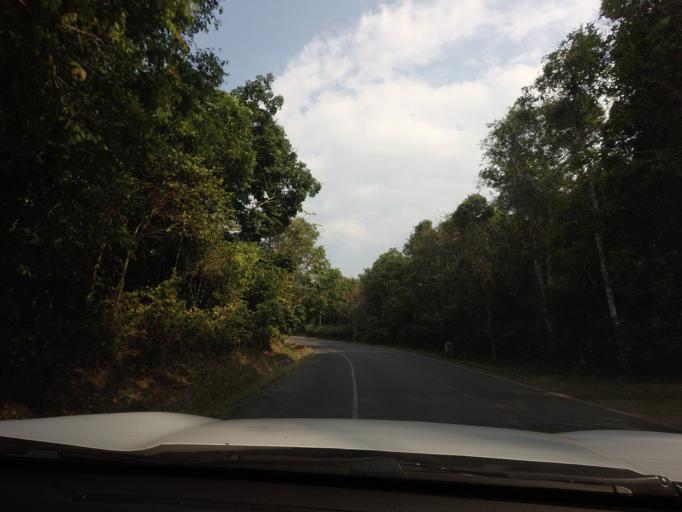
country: TH
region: Nakhon Nayok
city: Nakhon Nayok
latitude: 14.4125
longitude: 101.3762
